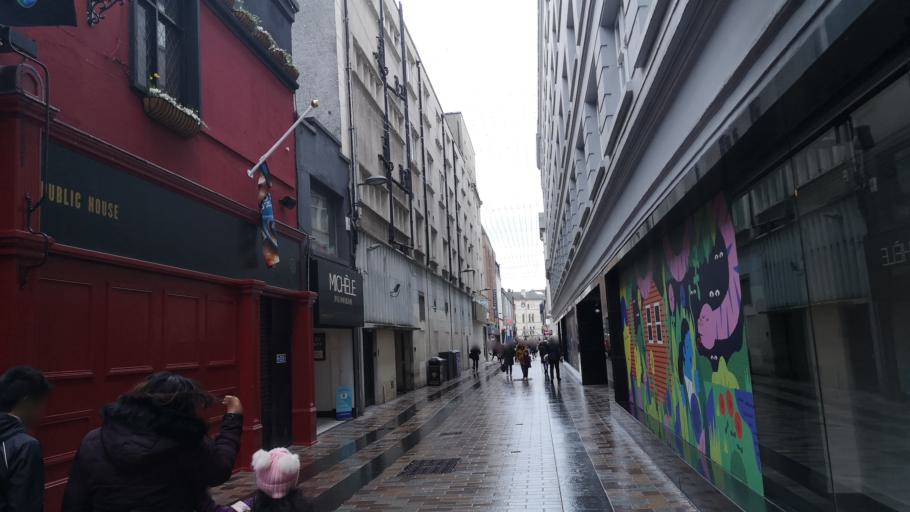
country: GB
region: Northern Ireland
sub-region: City of Belfast
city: Belfast
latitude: 54.5985
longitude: -5.9315
